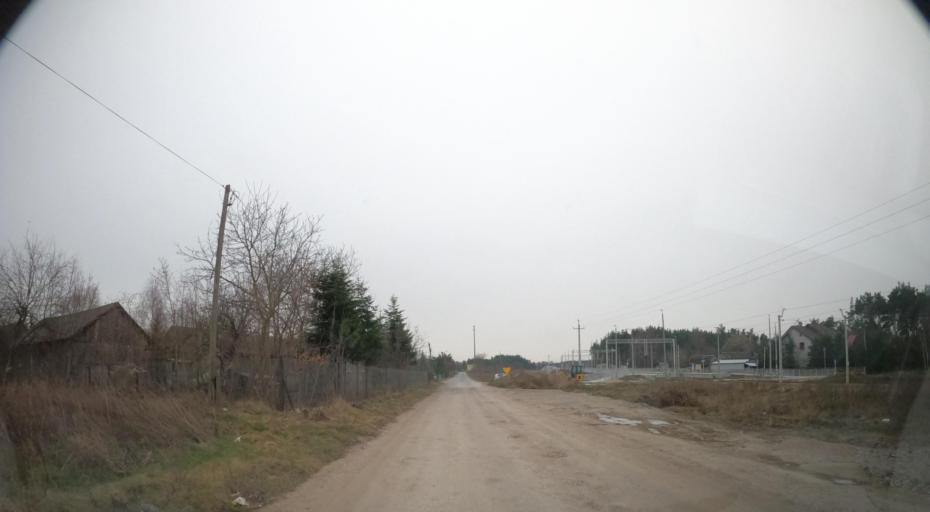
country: PL
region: Masovian Voivodeship
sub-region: Powiat radomski
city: Jastrzebia
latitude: 51.4808
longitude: 21.1939
